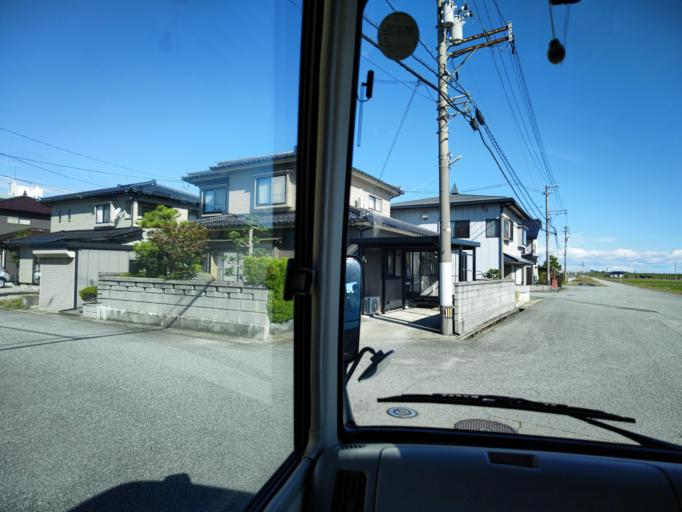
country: JP
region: Toyama
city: Nyuzen
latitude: 36.9094
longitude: 137.4283
